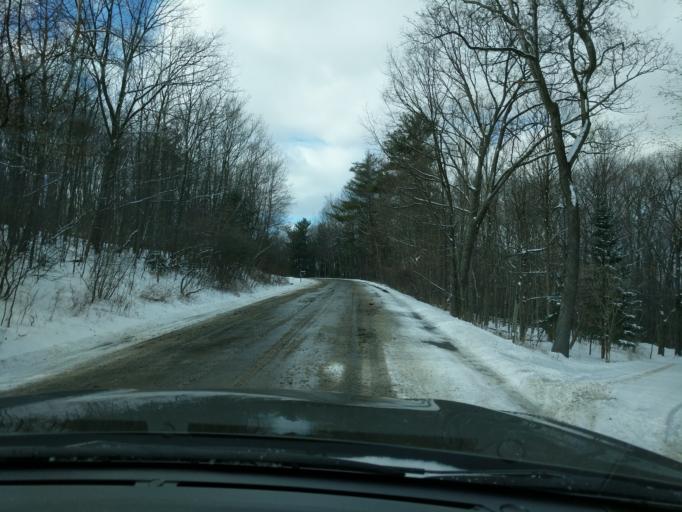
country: US
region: New York
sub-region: Tompkins County
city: East Ithaca
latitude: 42.4286
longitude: -76.4337
